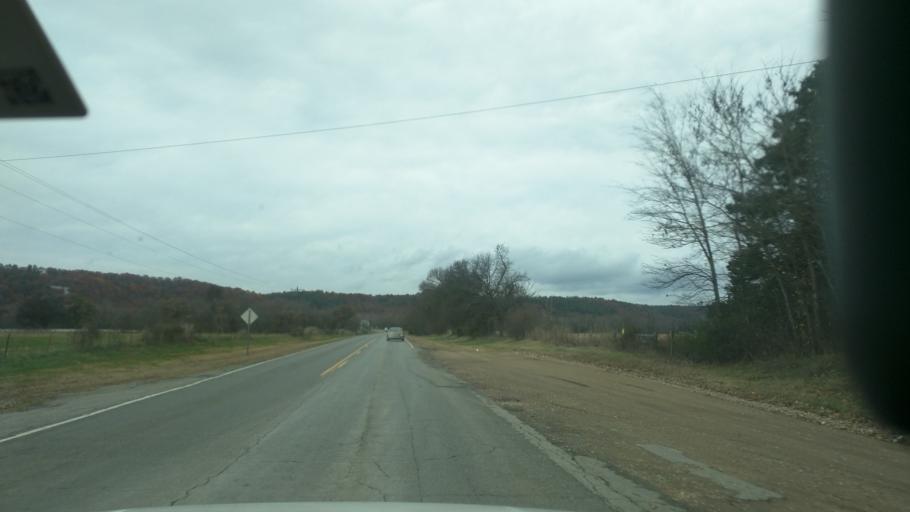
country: US
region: Oklahoma
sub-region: Cherokee County
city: Park Hill
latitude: 35.9147
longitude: -94.8344
